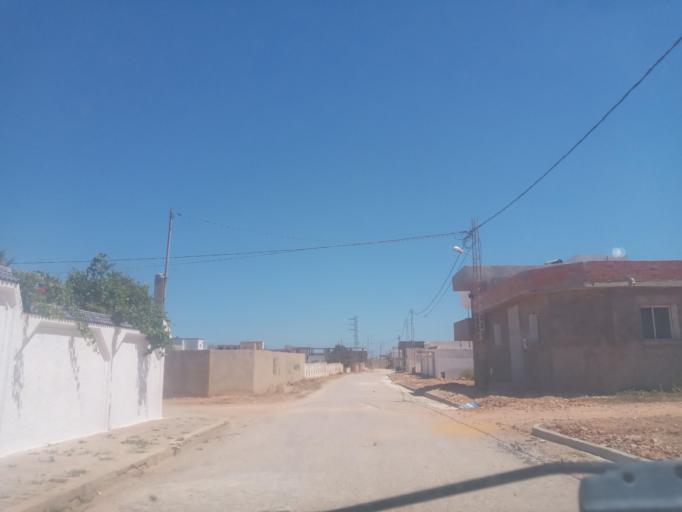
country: TN
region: Nabul
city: El Haouaria
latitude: 37.0565
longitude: 11.0042
